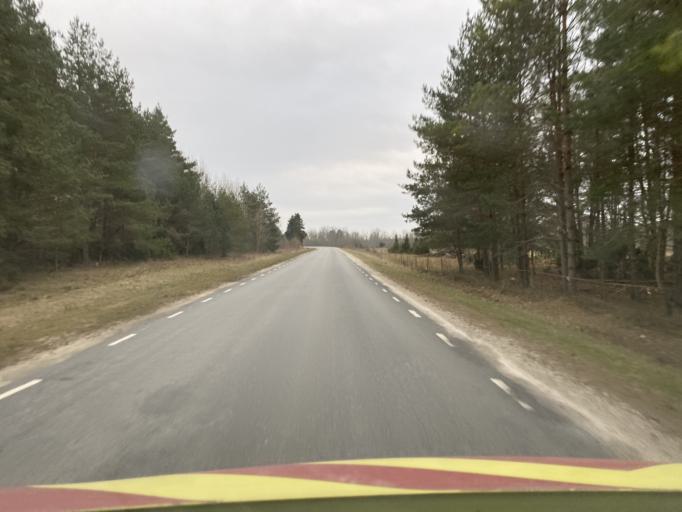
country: EE
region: Laeaene
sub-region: Ridala Parish
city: Uuemoisa
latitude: 59.0341
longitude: 23.6392
